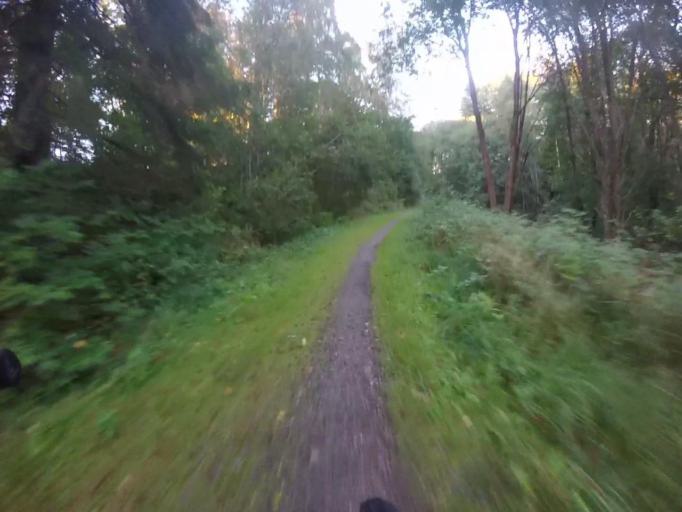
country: SE
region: Vaestra Goetaland
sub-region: Trollhattan
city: Trollhattan
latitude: 58.2807
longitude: 12.2612
